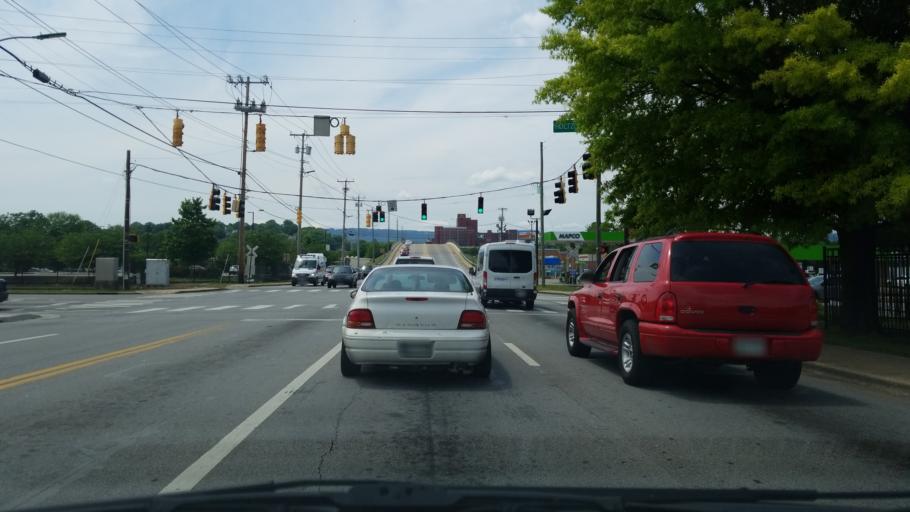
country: US
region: Tennessee
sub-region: Hamilton County
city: Chattanooga
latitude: 35.0437
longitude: -85.2795
